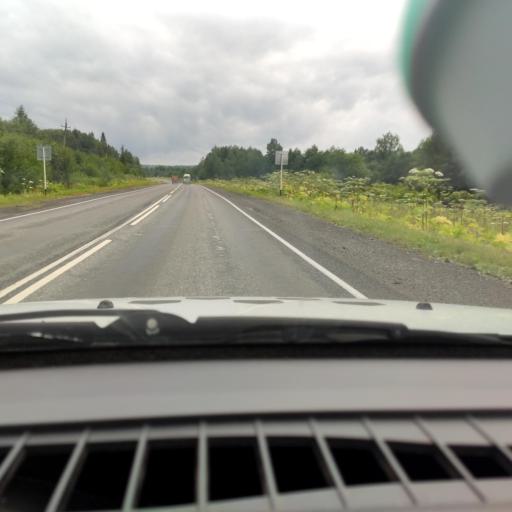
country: RU
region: Perm
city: Dobryanka
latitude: 58.8416
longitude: 56.7774
